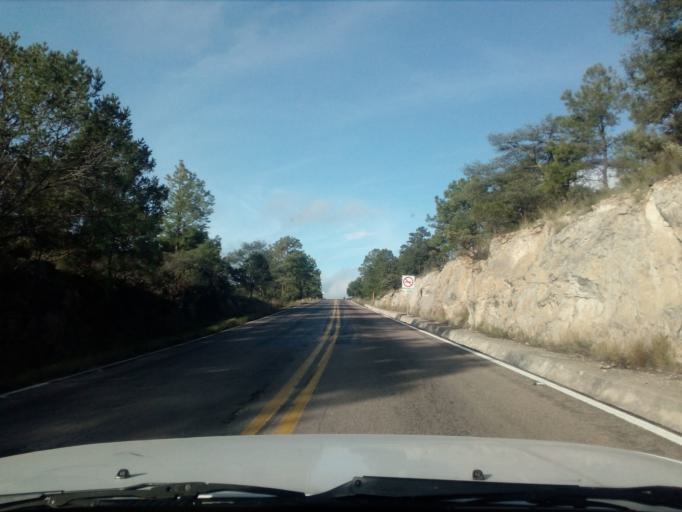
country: MX
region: Durango
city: Victoria de Durango
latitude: 23.9329
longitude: -104.9142
